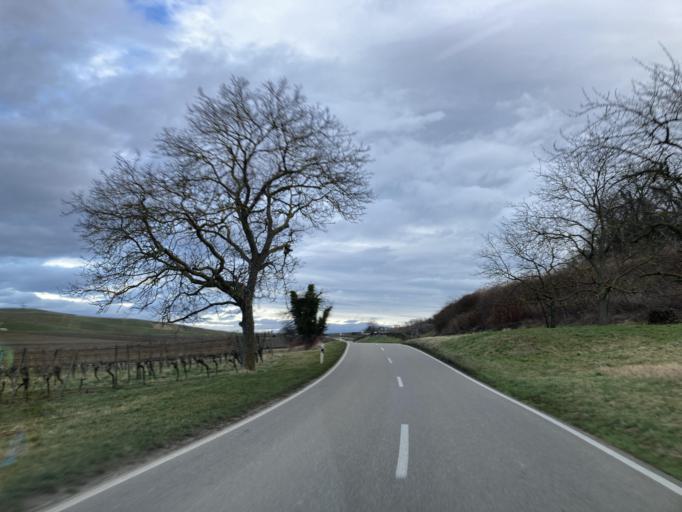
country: DE
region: Baden-Wuerttemberg
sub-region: Freiburg Region
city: Sasbach
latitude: 48.1164
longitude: 7.6260
